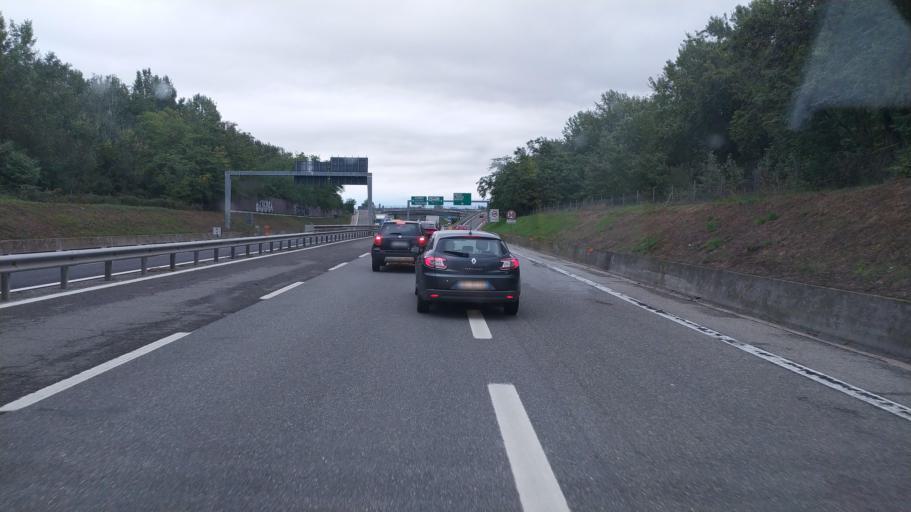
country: IT
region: Lombardy
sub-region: Provincia di Pavia
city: Pavia
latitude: 45.1964
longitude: 9.1364
